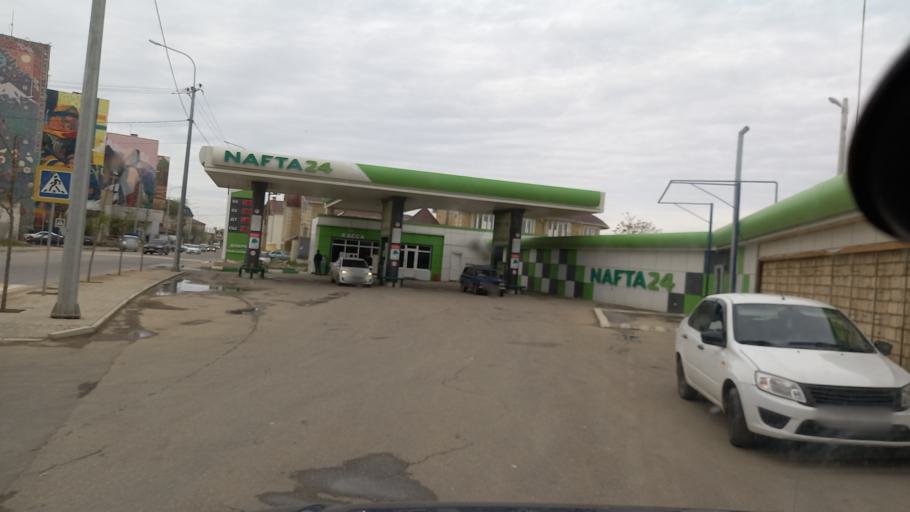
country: RU
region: Dagestan
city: Derbent
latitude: 42.0736
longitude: 48.2996
